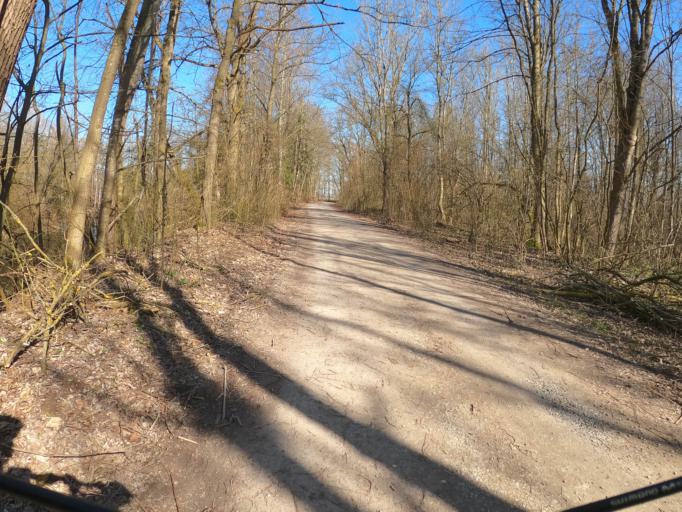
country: DE
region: Bavaria
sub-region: Swabia
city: Nersingen
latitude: 48.4470
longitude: 10.1371
